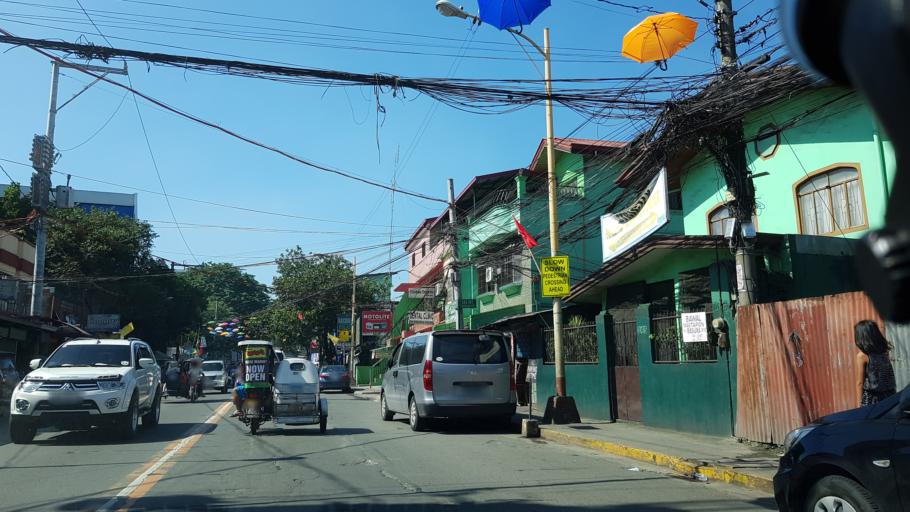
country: PH
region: Calabarzon
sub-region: Province of Rizal
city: Pateros
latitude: 14.5666
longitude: 121.0857
